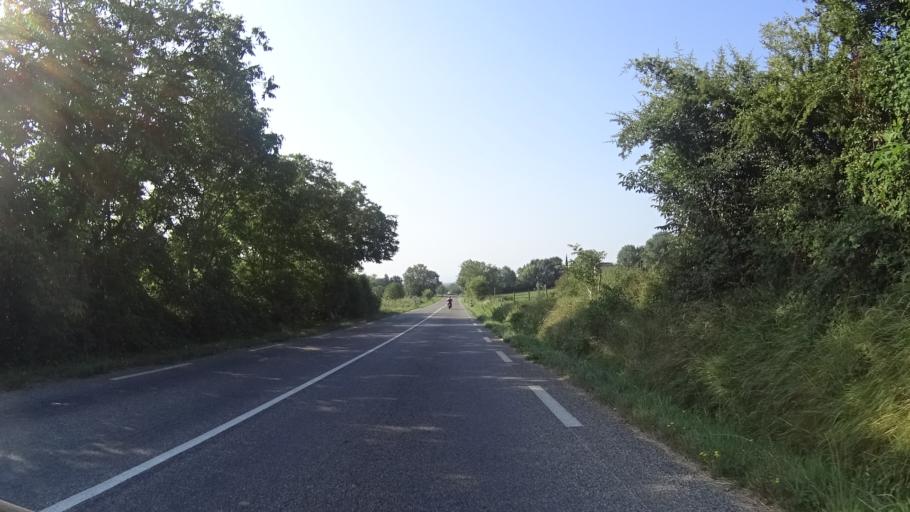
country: FR
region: Midi-Pyrenees
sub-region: Departement de l'Ariege
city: Mirepoix
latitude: 43.0769
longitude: 1.8775
